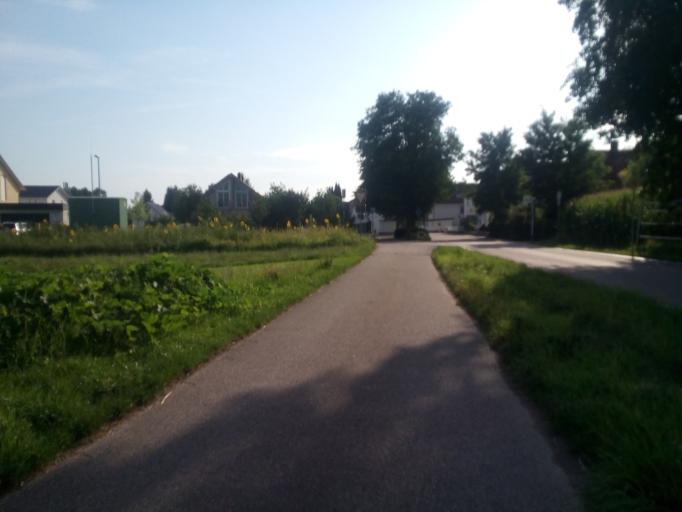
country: DE
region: Baden-Wuerttemberg
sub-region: Karlsruhe Region
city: Lichtenau
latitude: 48.7300
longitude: 8.0133
